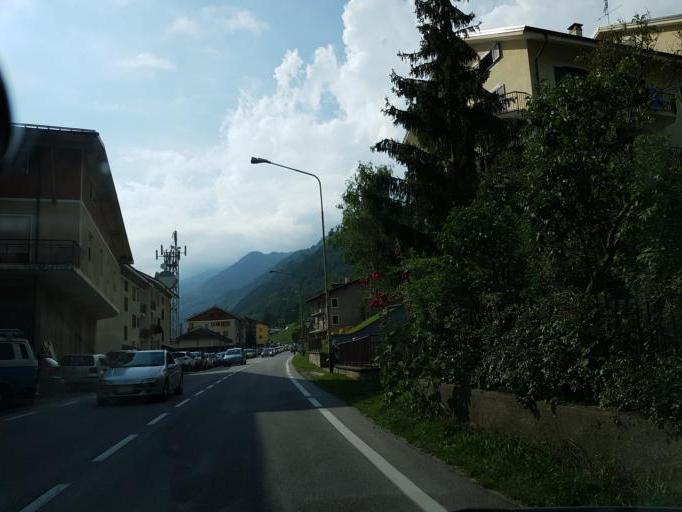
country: IT
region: Piedmont
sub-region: Provincia di Cuneo
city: Sampeyre
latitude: 44.5790
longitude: 7.1847
